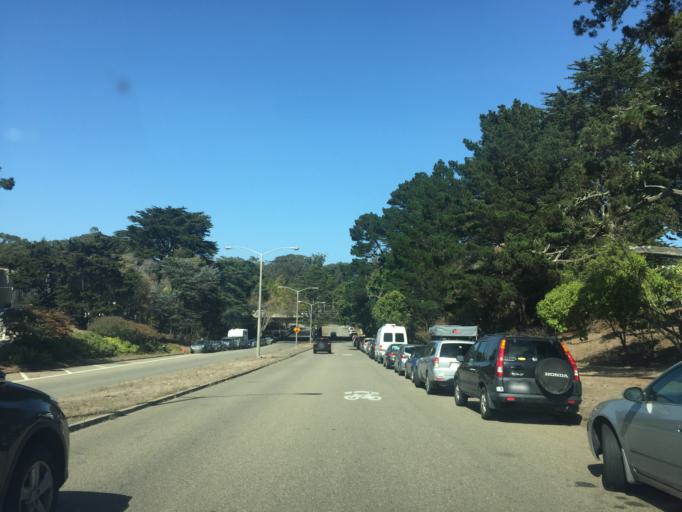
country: US
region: California
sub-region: San Mateo County
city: Daly City
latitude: 37.7631
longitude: -122.4959
